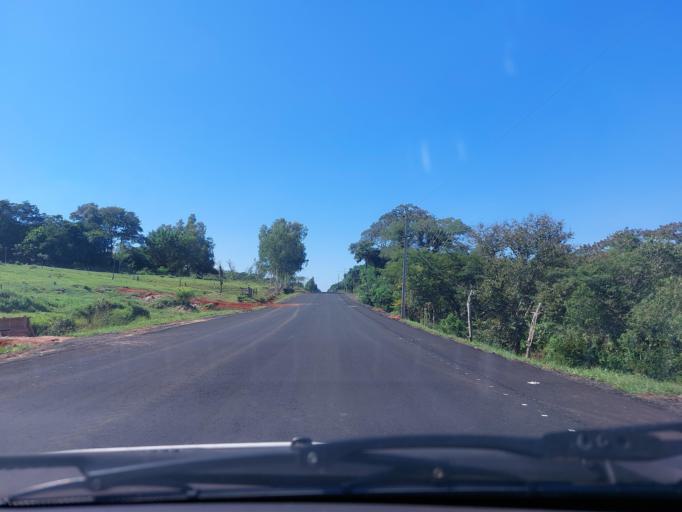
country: PY
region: San Pedro
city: Guayaybi
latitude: -24.5503
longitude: -56.5087
